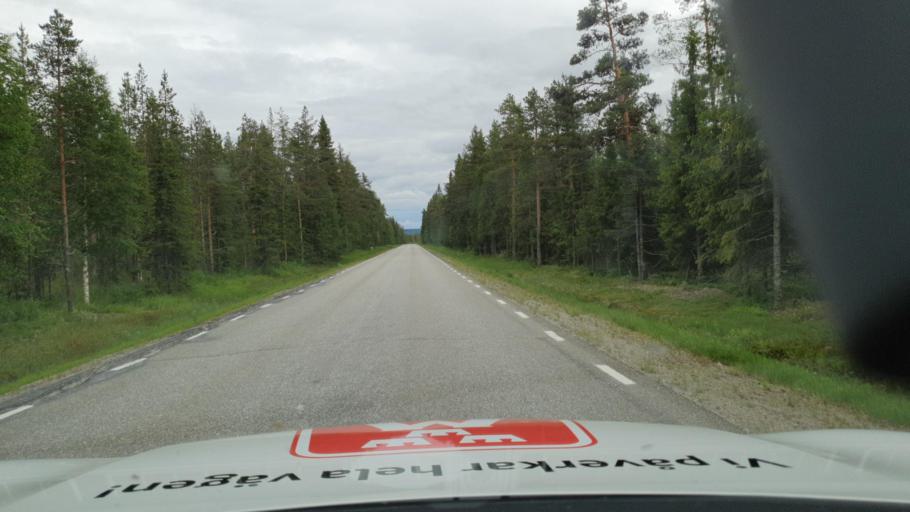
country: SE
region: Vaesterbotten
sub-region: Lycksele Kommun
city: Soderfors
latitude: 64.3120
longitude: 18.1630
